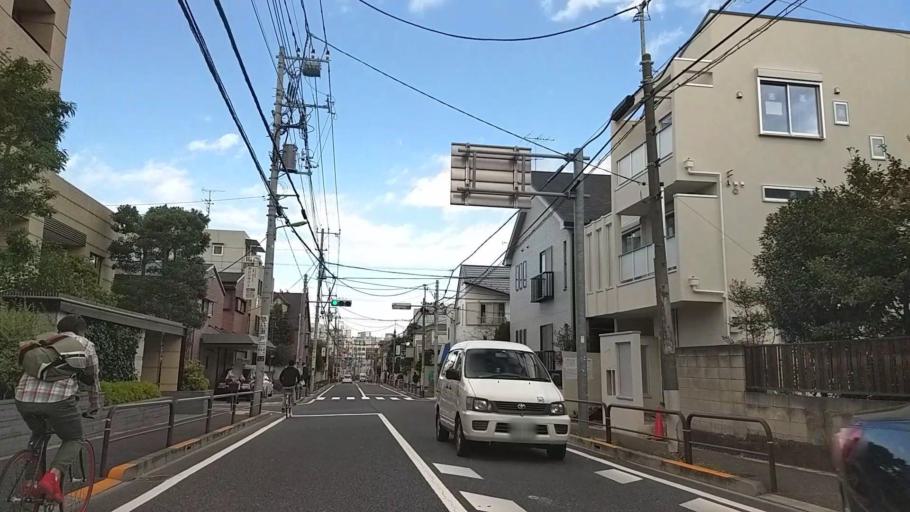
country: JP
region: Tokyo
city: Tokyo
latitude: 35.6516
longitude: 139.6672
